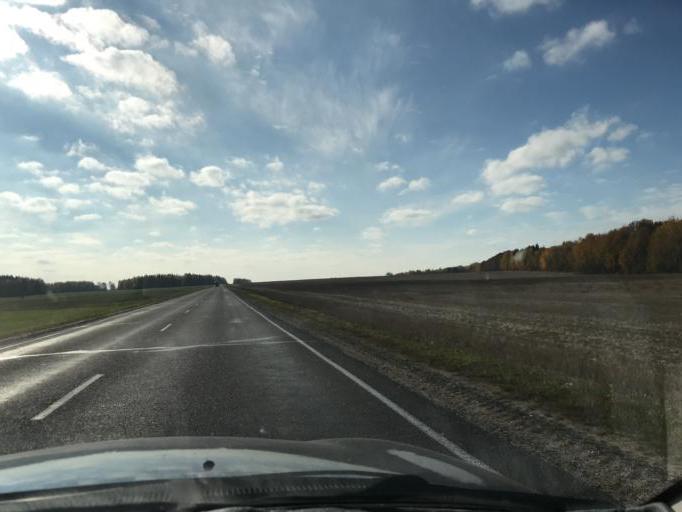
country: BY
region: Grodnenskaya
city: Voranava
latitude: 54.1990
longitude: 25.3471
